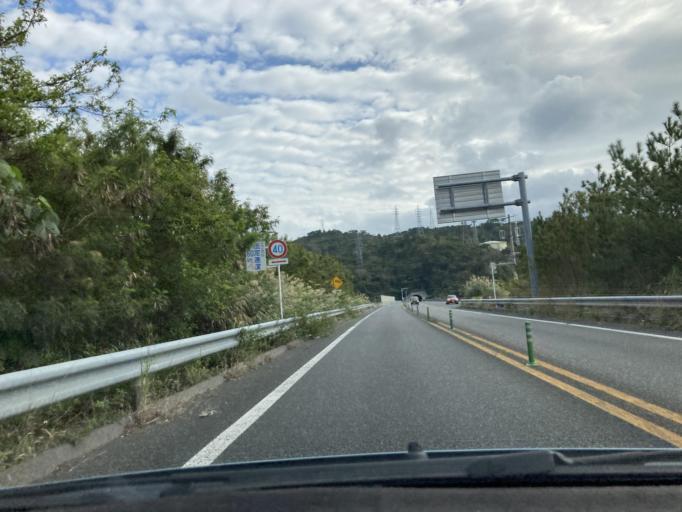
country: JP
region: Okinawa
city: Nago
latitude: 26.6055
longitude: 127.9991
